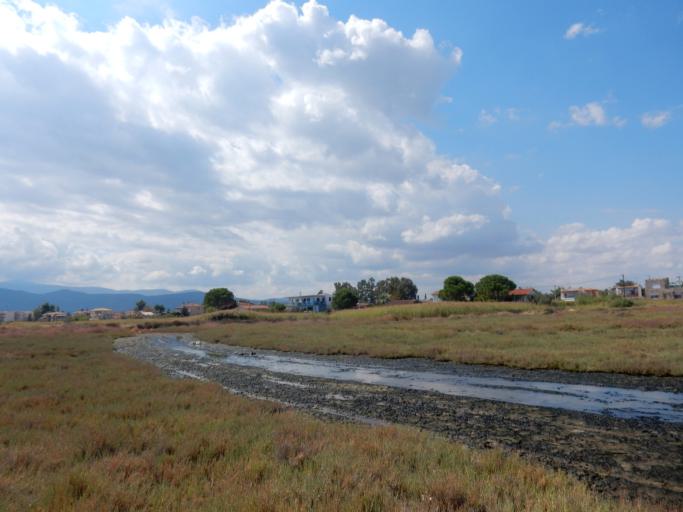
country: GR
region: Attica
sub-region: Nomarchia Anatolikis Attikis
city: Skala Oropou
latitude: 38.3340
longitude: 23.7771
